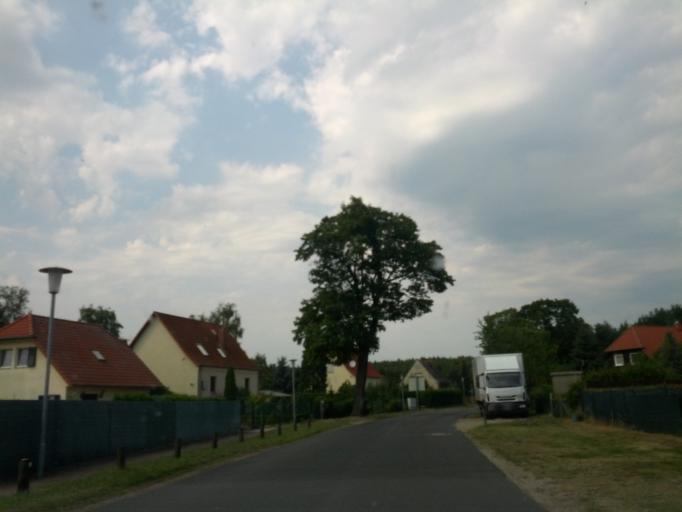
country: DE
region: Brandenburg
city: Nauen
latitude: 52.6879
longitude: 12.9364
